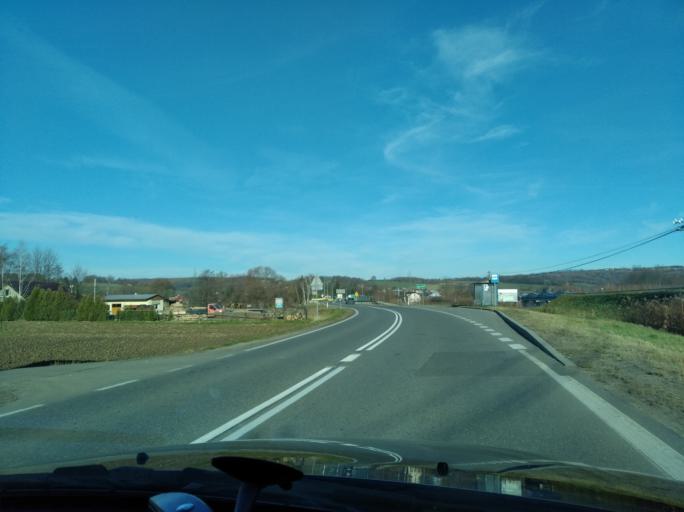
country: PL
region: Subcarpathian Voivodeship
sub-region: Powiat strzyzowski
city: Czudec
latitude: 49.9329
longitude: 21.8176
